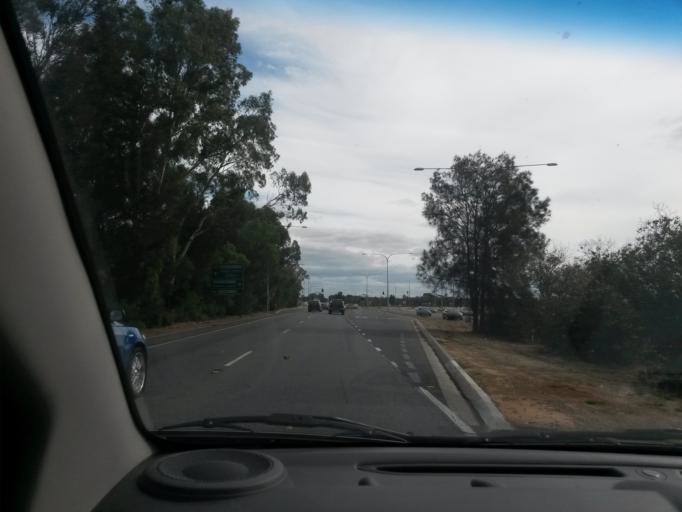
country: AU
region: South Australia
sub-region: Salisbury
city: Ingle Farm
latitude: -34.8074
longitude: 138.6330
